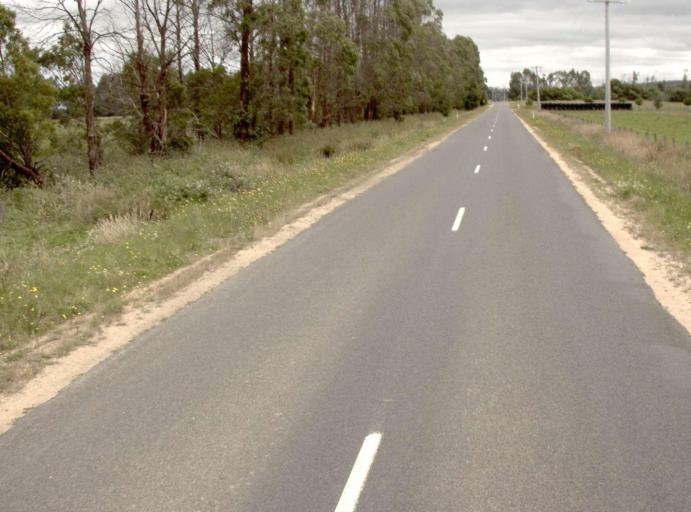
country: AU
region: Victoria
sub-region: Latrobe
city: Traralgon
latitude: -38.4984
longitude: 146.6759
